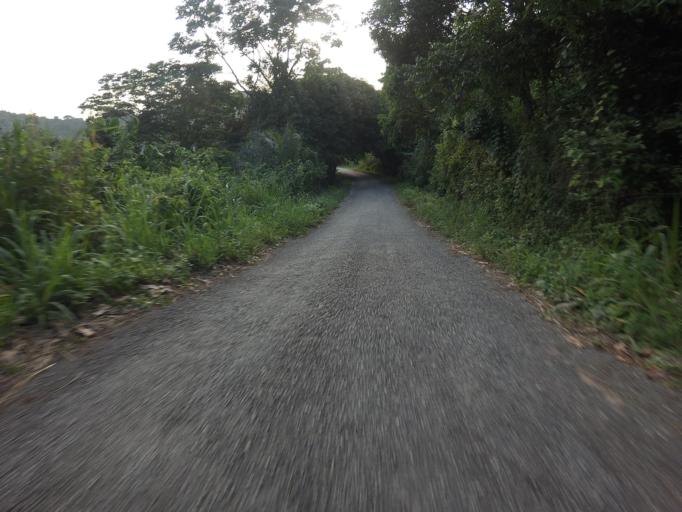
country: GH
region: Volta
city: Kpandu
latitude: 6.8796
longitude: 0.4430
